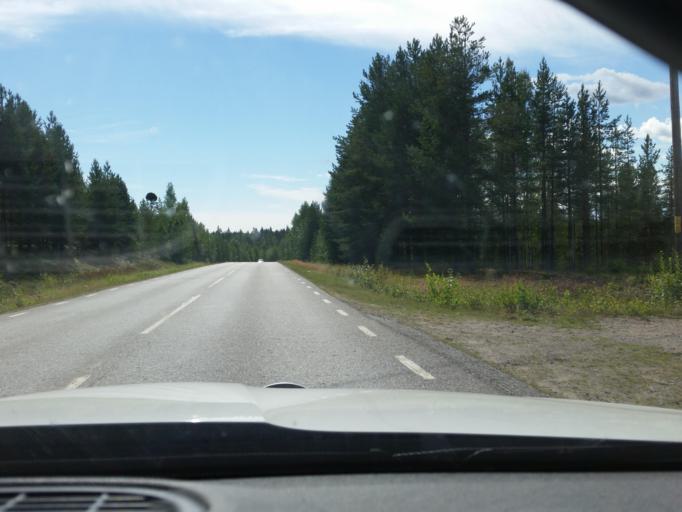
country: SE
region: Norrbotten
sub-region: Pitea Kommun
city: Norrfjarden
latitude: 65.4543
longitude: 21.4560
